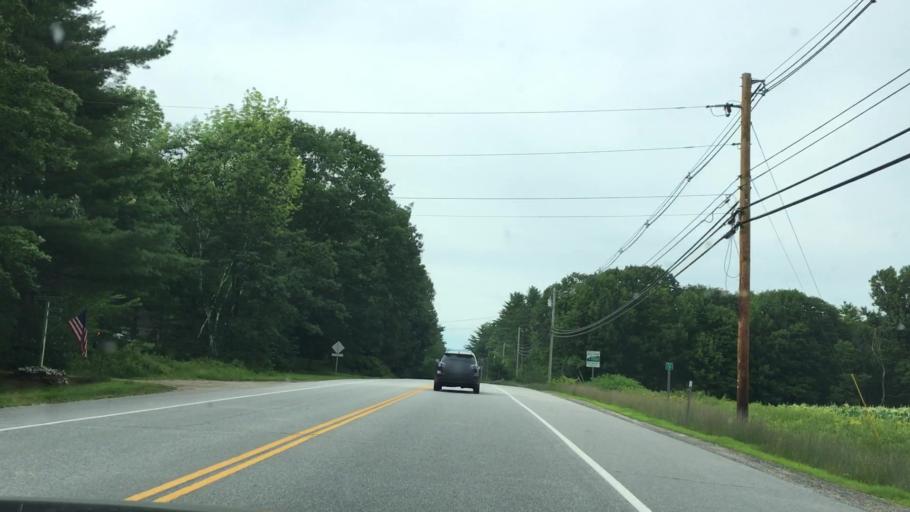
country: US
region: New Hampshire
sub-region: Carroll County
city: Center Harbor
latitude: 43.6890
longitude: -71.4583
